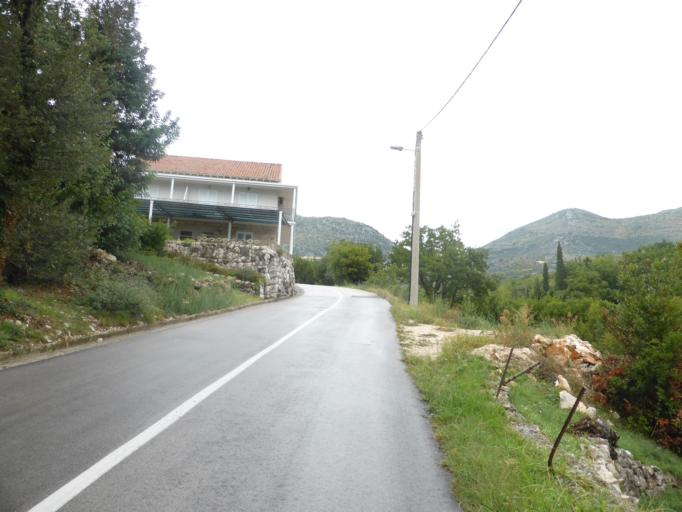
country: HR
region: Dubrovacko-Neretvanska
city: Podgora
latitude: 42.7859
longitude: 17.8790
